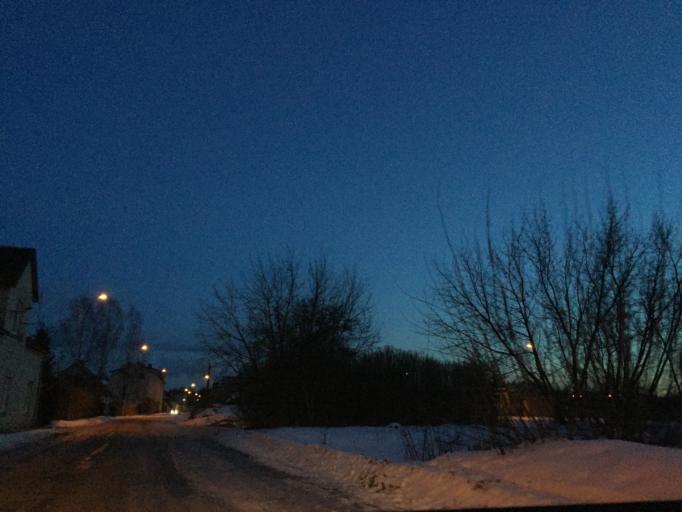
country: LV
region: Jaunjelgava
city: Jaunjelgava
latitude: 56.6199
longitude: 25.0883
